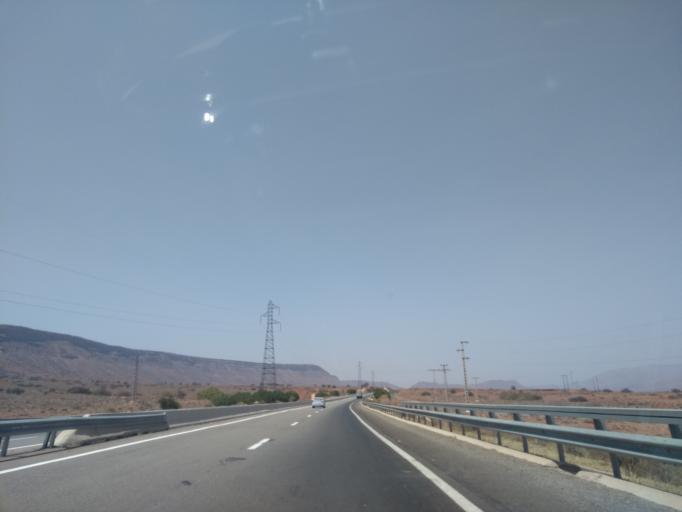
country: MA
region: Marrakech-Tensift-Al Haouz
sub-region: Chichaoua
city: Timezgadiouine
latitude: 30.8876
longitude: -9.0781
